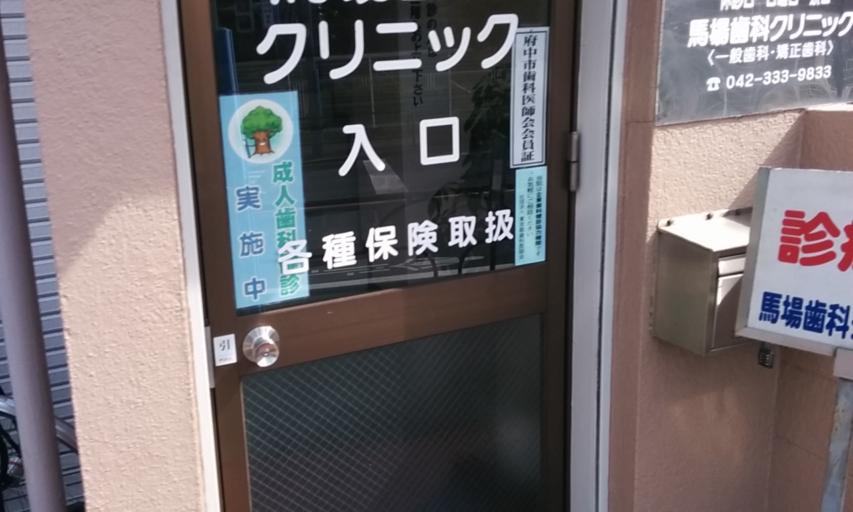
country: JP
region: Tokyo
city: Kokubunji
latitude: 35.6817
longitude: 139.4718
